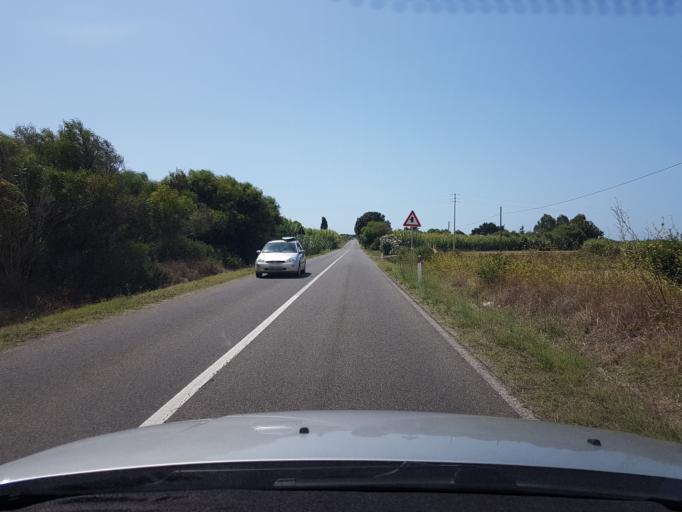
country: IT
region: Sardinia
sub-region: Provincia di Oristano
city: Riola Sardo
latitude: 40.0225
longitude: 8.4736
